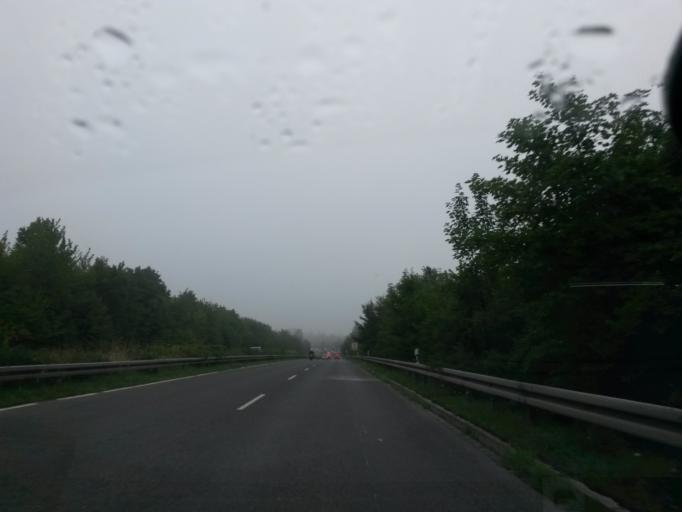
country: DE
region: Bavaria
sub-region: Regierungsbezirk Mittelfranken
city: Zirndorf
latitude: 49.4493
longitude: 10.9753
